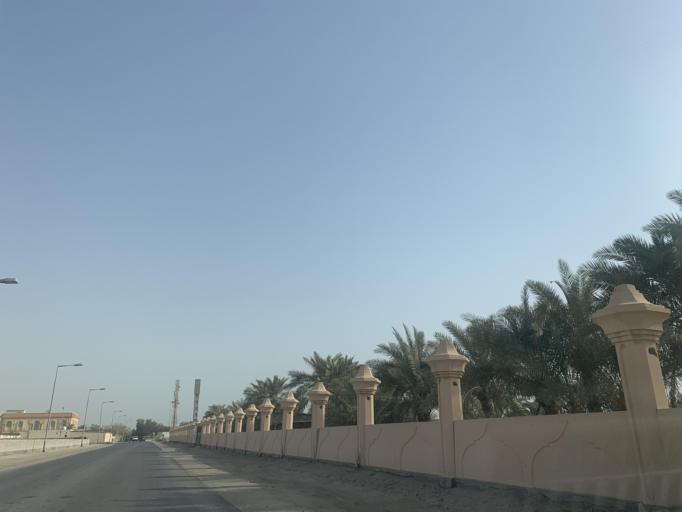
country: BH
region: Central Governorate
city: Madinat Hamad
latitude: 26.1778
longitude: 50.4677
